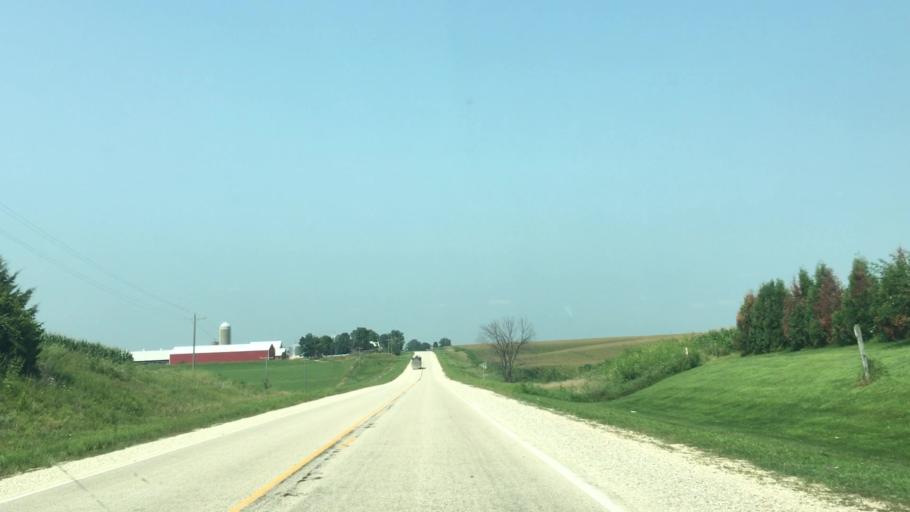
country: US
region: Iowa
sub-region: Fayette County
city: West Union
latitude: 43.0097
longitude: -91.8242
